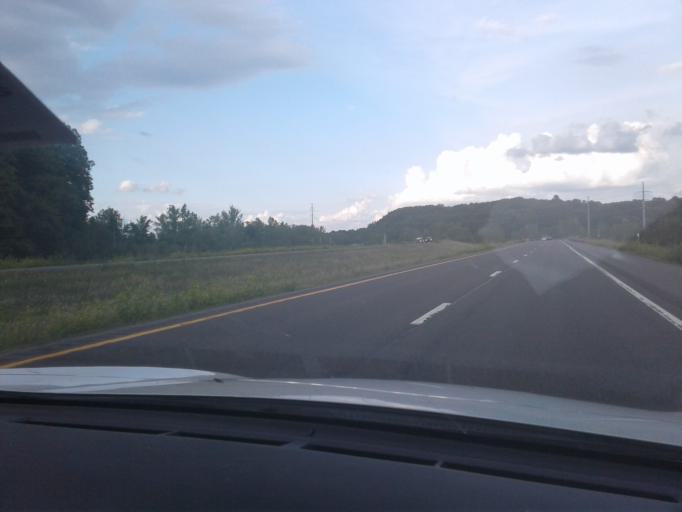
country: US
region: New York
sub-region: Onondaga County
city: East Syracuse
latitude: 43.0110
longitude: -76.0788
